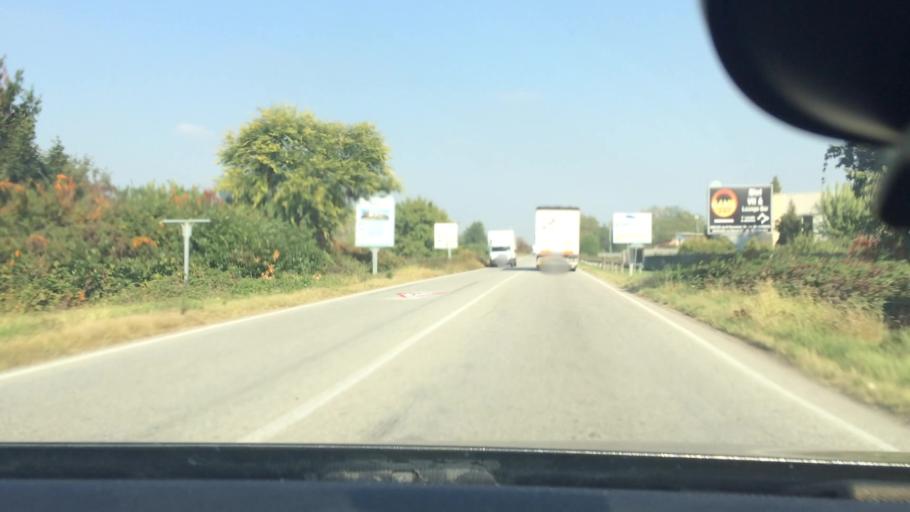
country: IT
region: Lombardy
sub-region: Citta metropolitana di Milano
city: Sedriano
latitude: 45.4991
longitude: 8.9622
